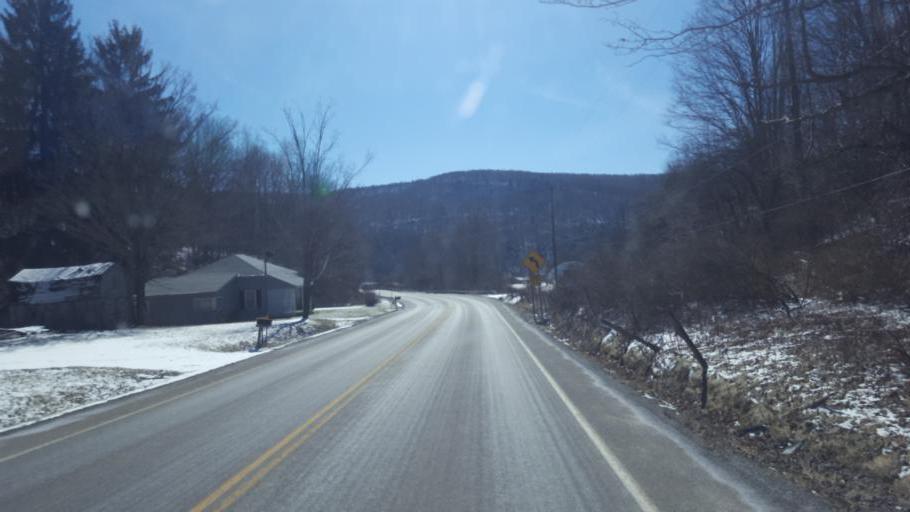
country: US
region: New York
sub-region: Allegany County
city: Andover
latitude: 42.0404
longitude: -77.7856
